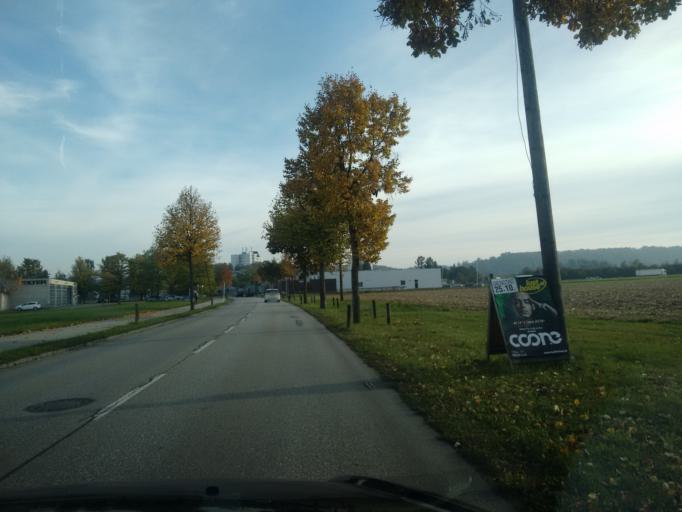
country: AT
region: Upper Austria
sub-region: Wels-Land
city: Gunskirchen
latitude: 48.1504
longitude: 13.9873
